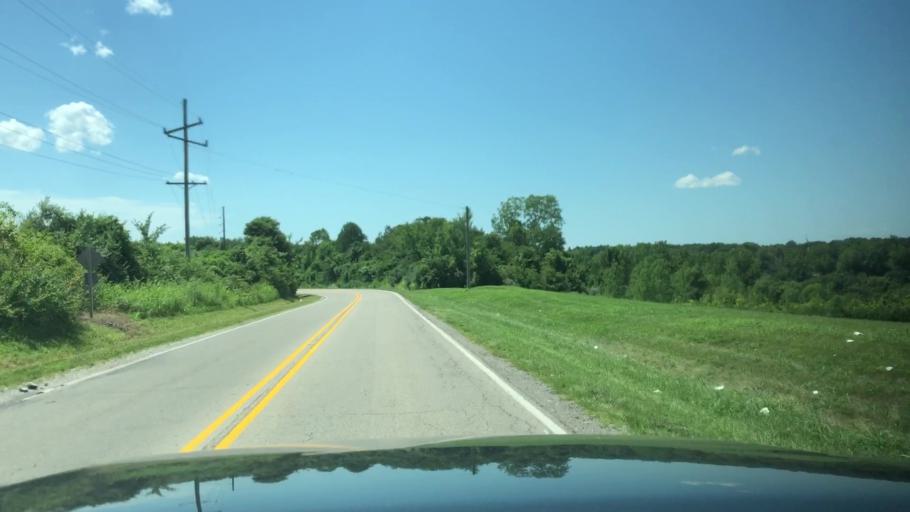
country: US
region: Illinois
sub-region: Saint Clair County
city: Centreville
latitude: 38.5539
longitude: -90.0814
